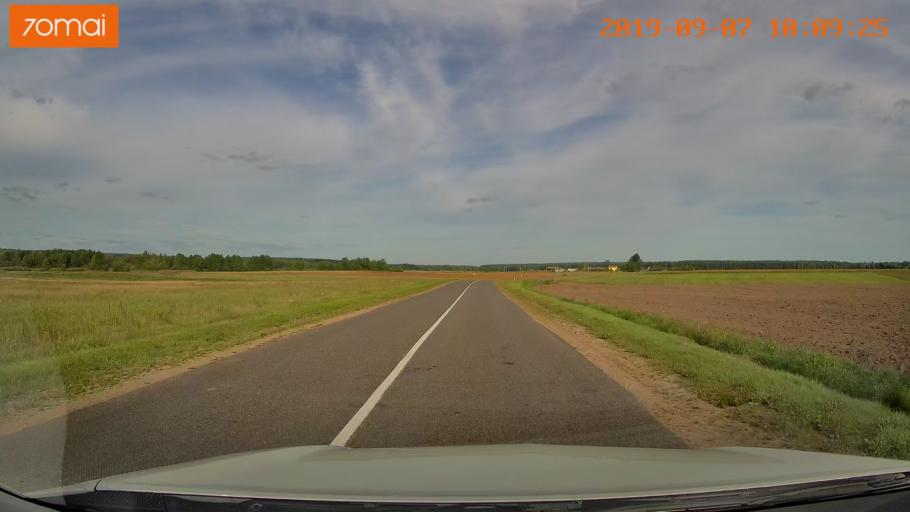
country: BY
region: Grodnenskaya
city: Voranava
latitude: 54.0954
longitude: 25.3737
